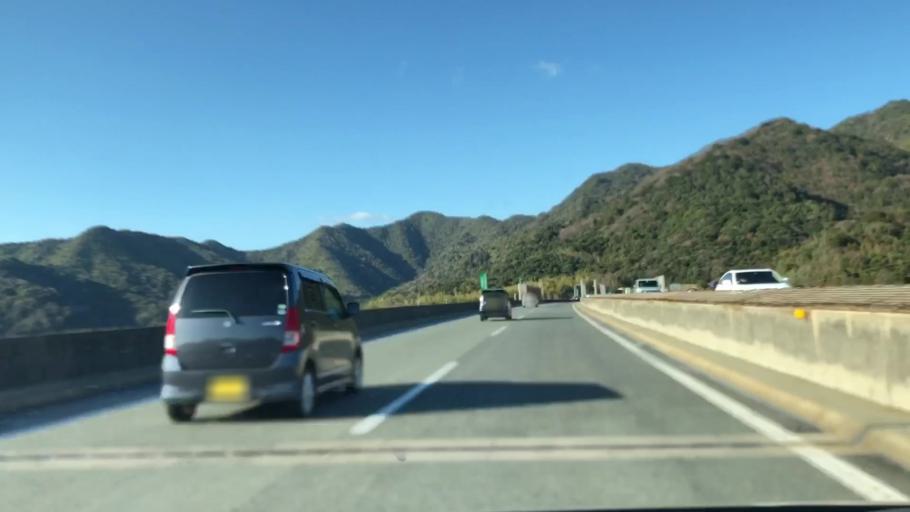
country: JP
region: Yamaguchi
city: Ogori-shimogo
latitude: 34.0958
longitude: 131.4537
